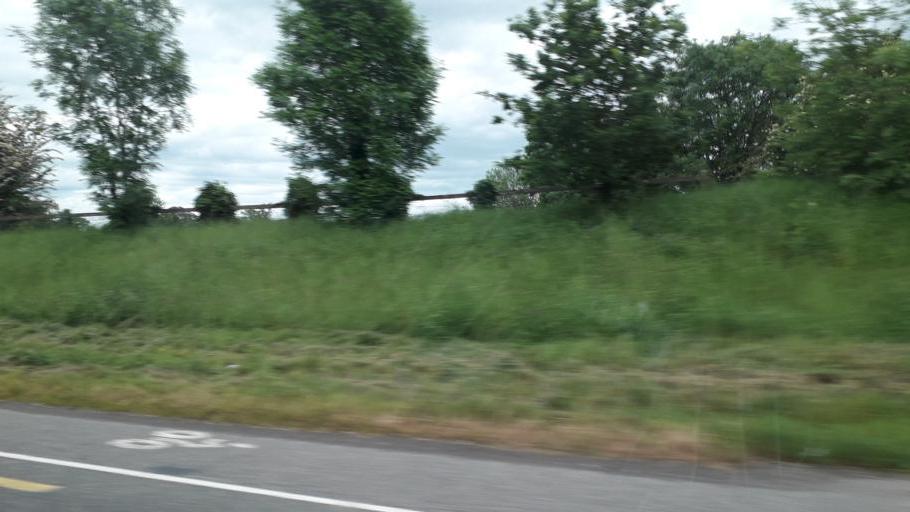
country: IE
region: Leinster
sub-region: County Carlow
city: Bagenalstown
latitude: 52.7402
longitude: -6.9844
